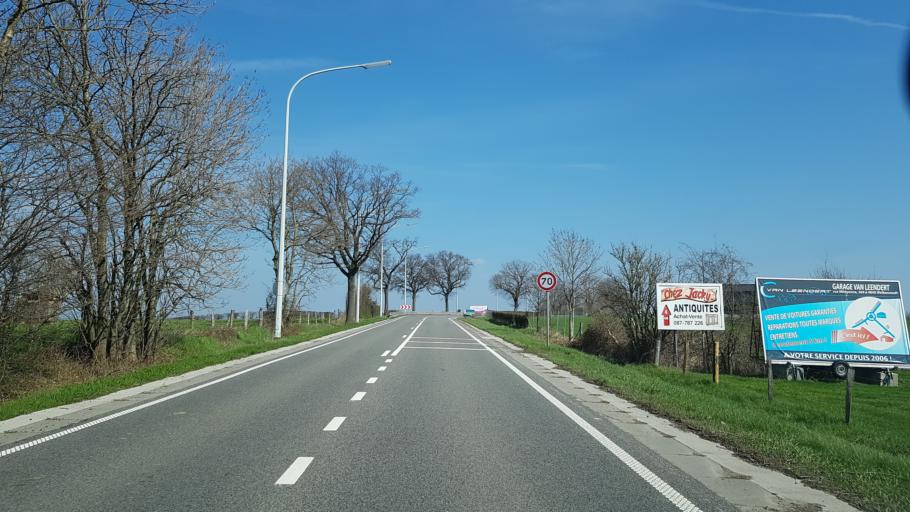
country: BE
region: Wallonia
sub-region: Province de Liege
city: Aubel
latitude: 50.6662
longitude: 5.8978
